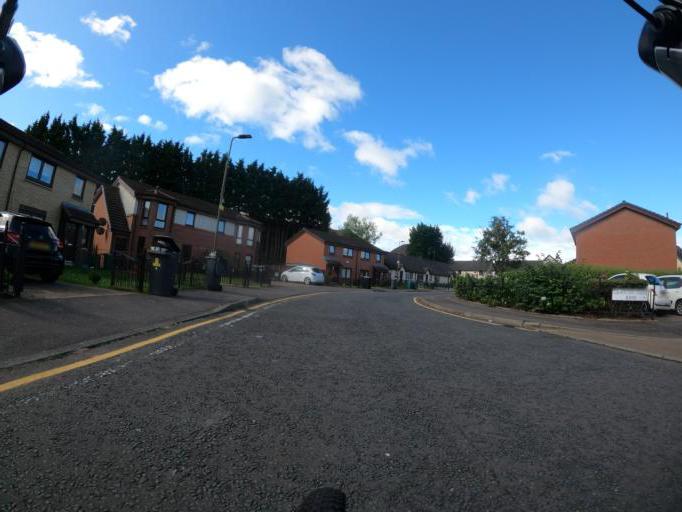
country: GB
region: Scotland
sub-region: Edinburgh
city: Edinburgh
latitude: 55.9758
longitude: -3.2464
